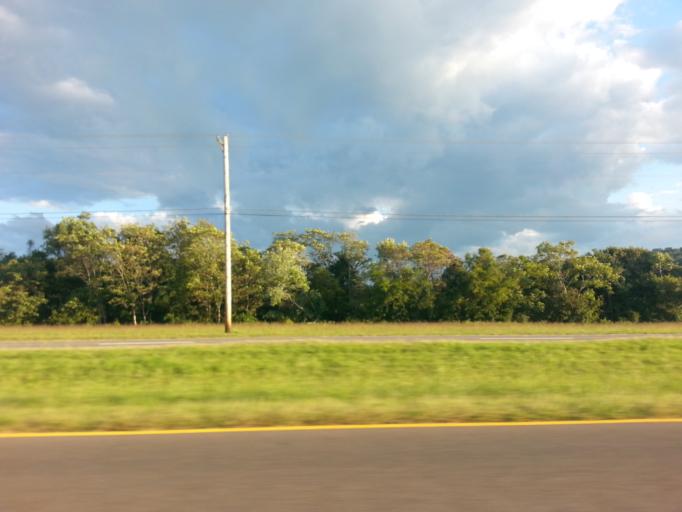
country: US
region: Tennessee
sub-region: Jefferson County
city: New Market
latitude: 36.1034
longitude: -83.5444
